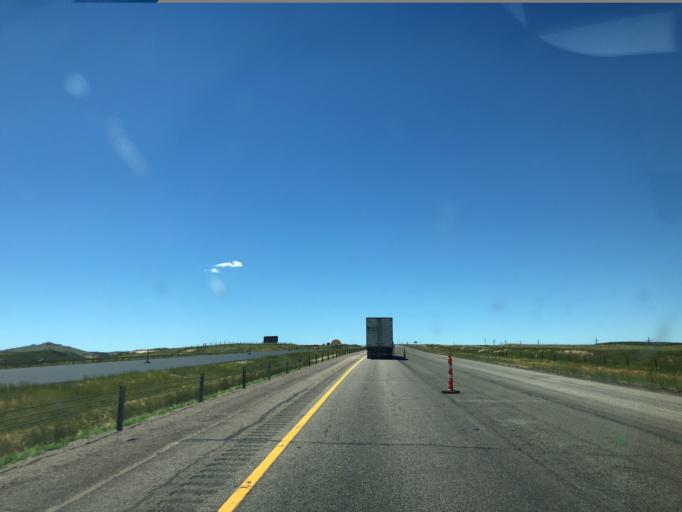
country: US
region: Wyoming
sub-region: Laramie County
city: Cheyenne
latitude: 41.0989
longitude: -105.1383
